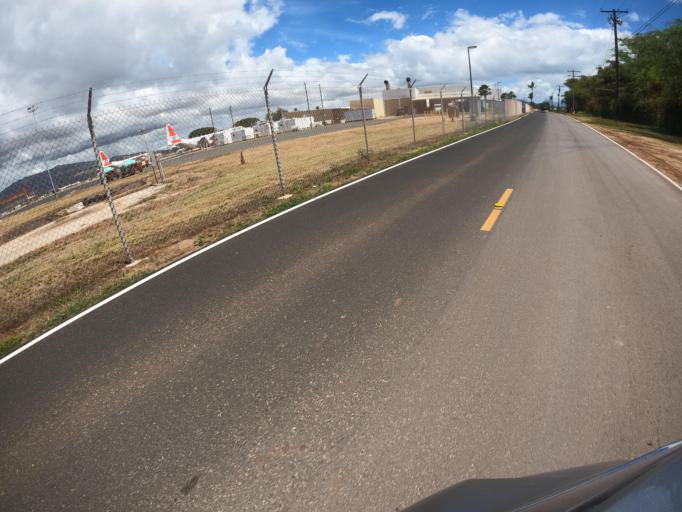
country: US
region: Hawaii
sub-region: Honolulu County
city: Makakilo City
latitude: 21.2992
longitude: -158.0721
